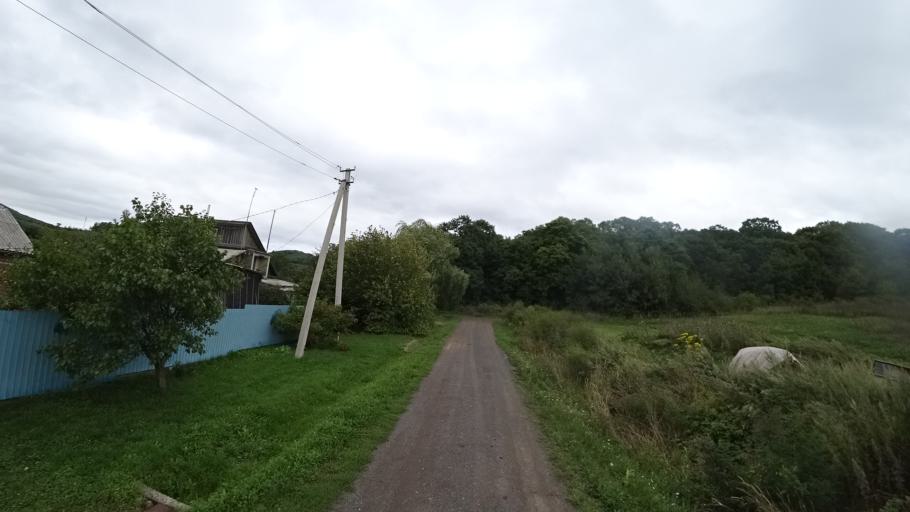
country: RU
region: Primorskiy
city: Chernigovka
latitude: 44.4584
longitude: 132.5975
